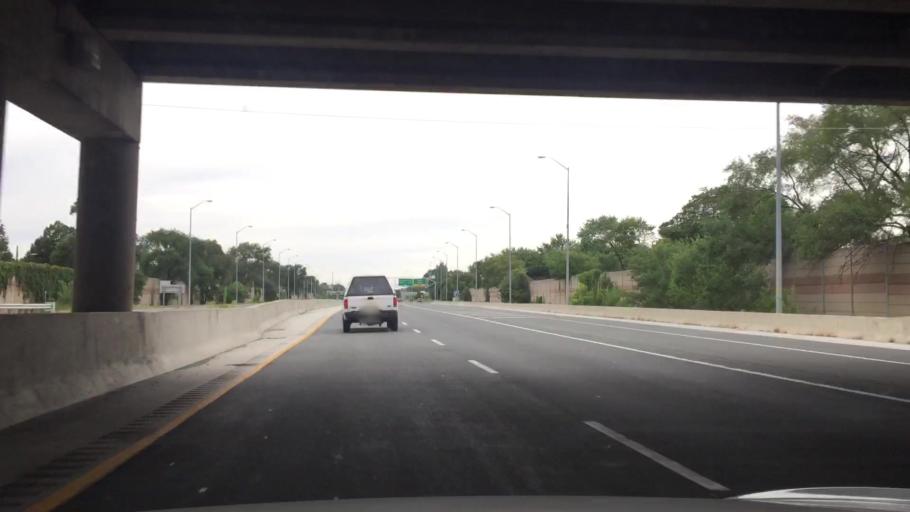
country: CA
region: Ontario
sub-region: Lambton County
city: Sarnia
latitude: 42.9867
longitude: -82.3663
